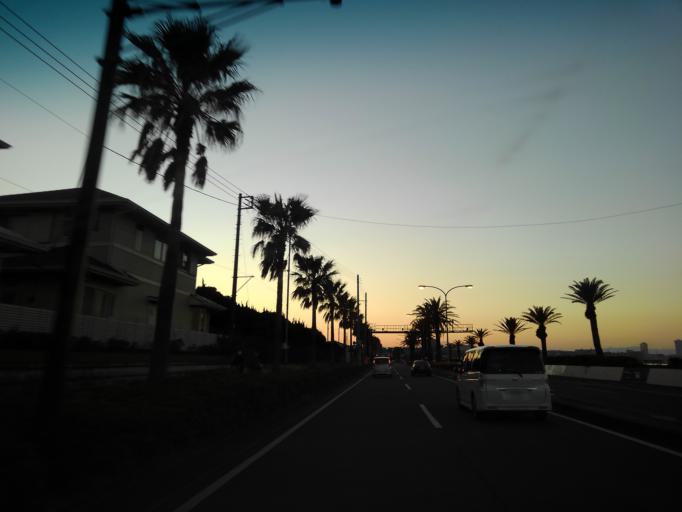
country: JP
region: Kanagawa
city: Yokosuka
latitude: 35.2635
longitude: 139.7079
